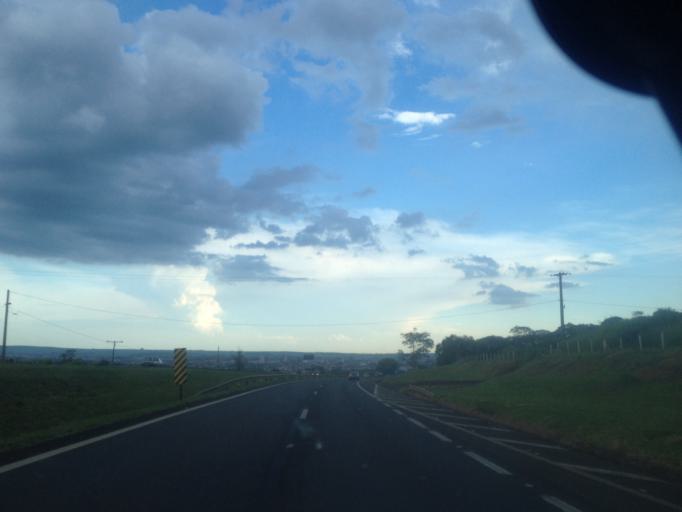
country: BR
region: Sao Paulo
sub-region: Leme
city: Leme
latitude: -22.1514
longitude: -47.4011
